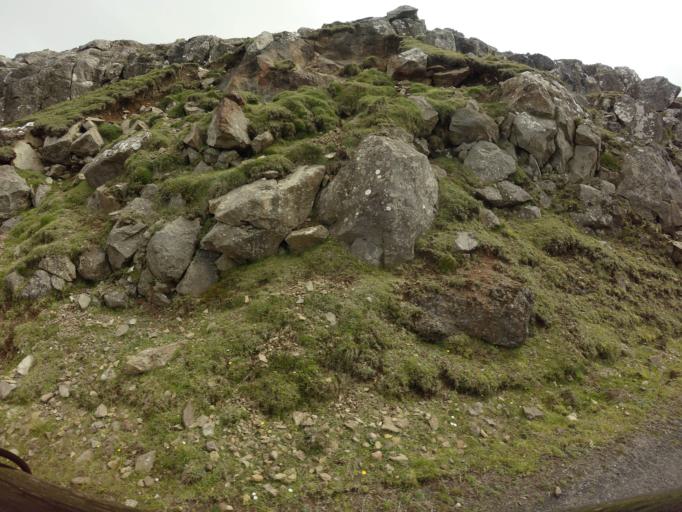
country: FO
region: Sandoy
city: Sandur
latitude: 61.8015
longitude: -6.7531
